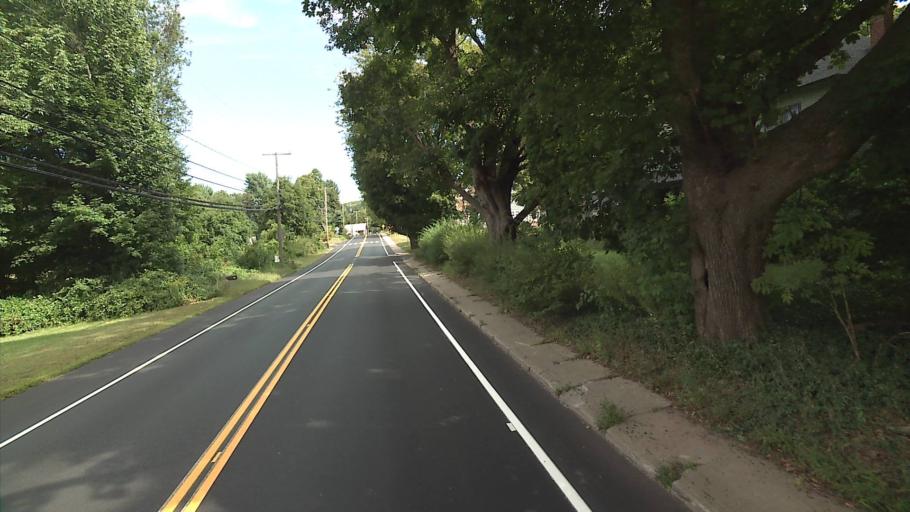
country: US
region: Connecticut
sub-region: Tolland County
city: Storrs
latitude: 41.8527
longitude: -72.3014
